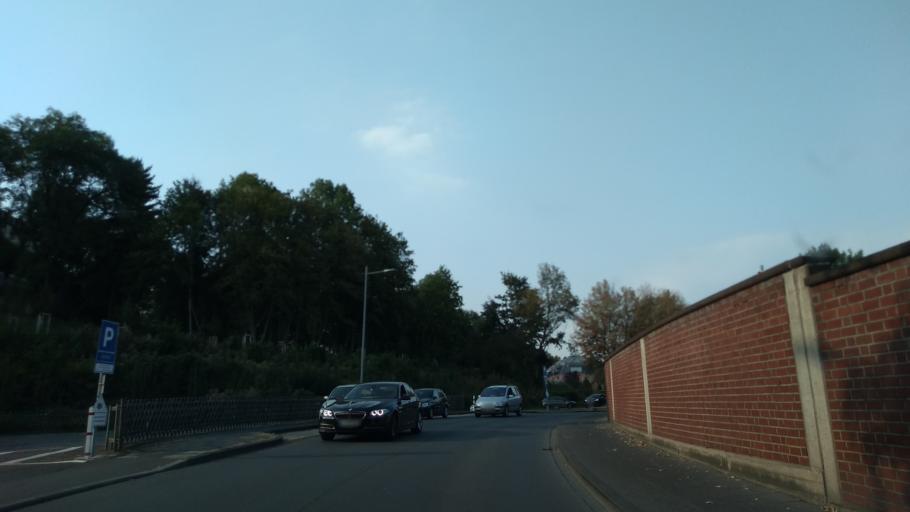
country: DE
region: North Rhine-Westphalia
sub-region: Regierungsbezirk Koln
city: Siegburg
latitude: 50.7946
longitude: 7.2137
